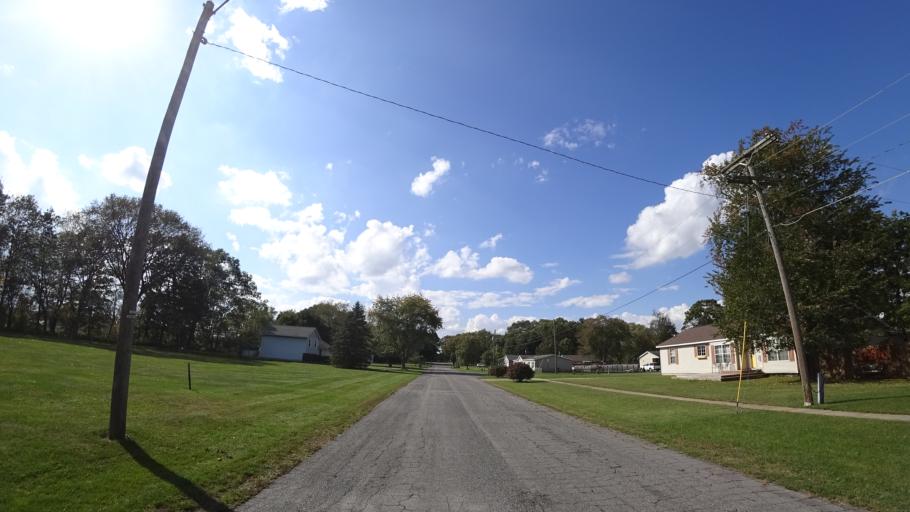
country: US
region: Michigan
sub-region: Saint Joseph County
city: Three Rivers
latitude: 41.9516
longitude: -85.6115
